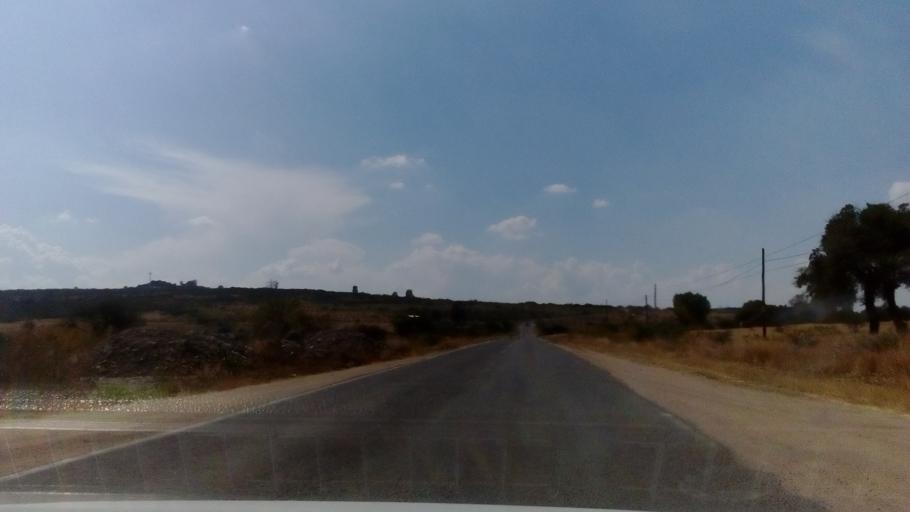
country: MX
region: Guanajuato
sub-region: Silao de la Victoria
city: San Francisco (Banos de Agua Caliente)
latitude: 21.0759
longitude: -101.4804
